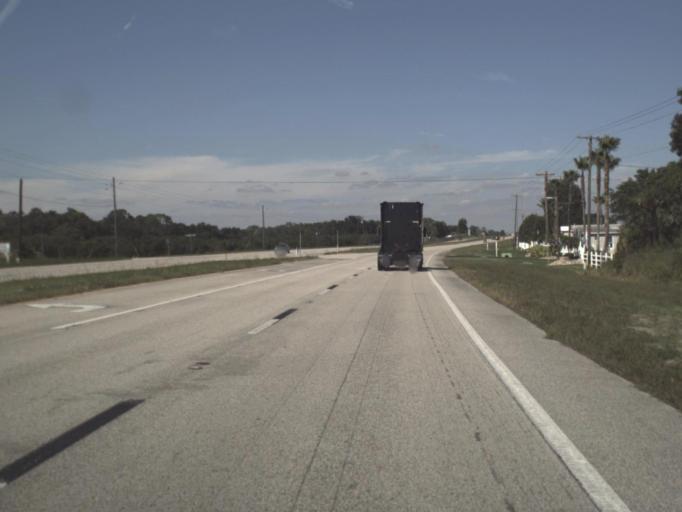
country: US
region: Florida
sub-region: Highlands County
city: Sebring
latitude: 27.3973
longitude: -81.4163
